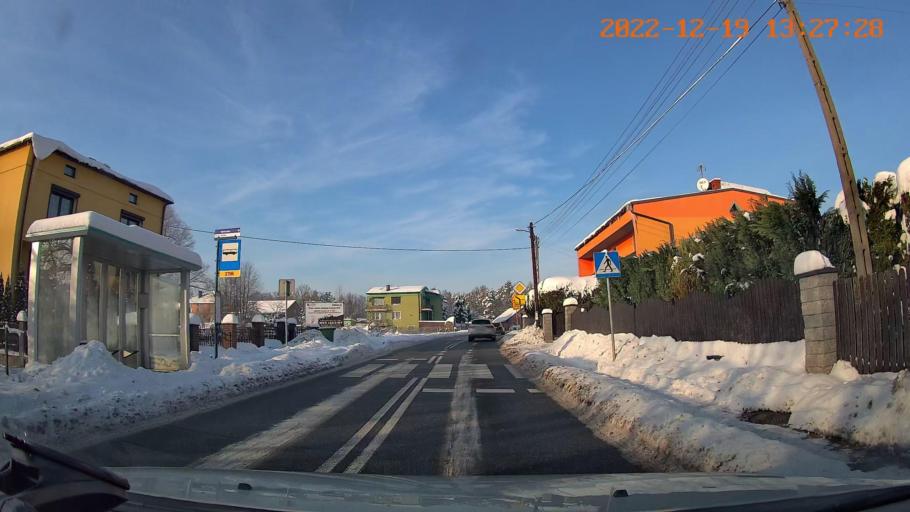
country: PL
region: Silesian Voivodeship
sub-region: Powiat bierunsko-ledzinski
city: Ledziny
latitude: 50.1074
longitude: 19.1361
